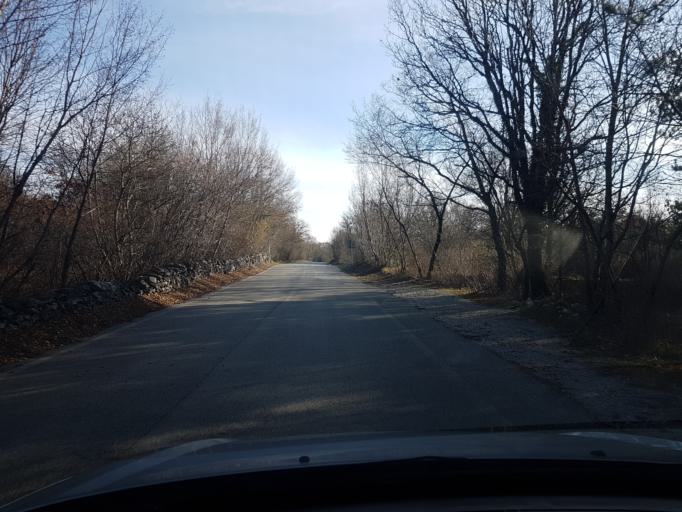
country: IT
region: Friuli Venezia Giulia
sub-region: Provincia di Trieste
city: Aurisina Cave
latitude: 45.7798
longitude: 13.6722
